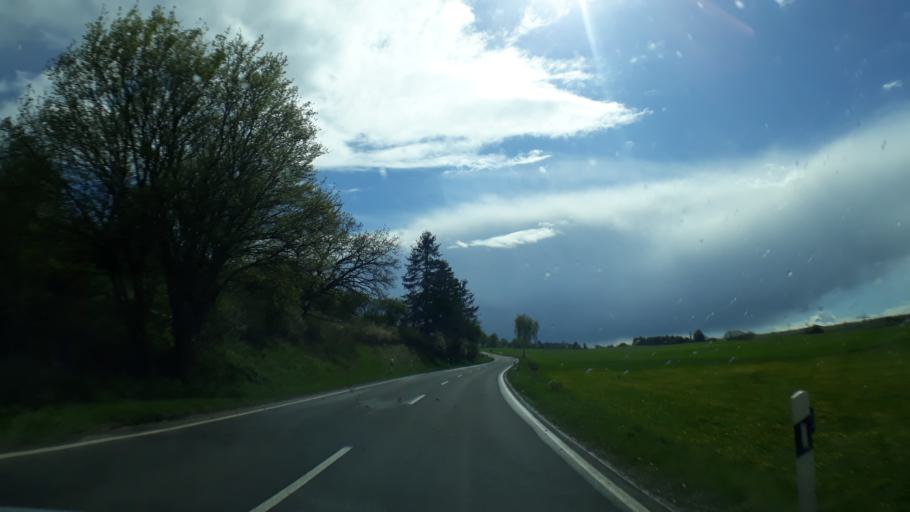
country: DE
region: North Rhine-Westphalia
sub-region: Regierungsbezirk Koln
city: Kall
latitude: 50.5035
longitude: 6.5347
